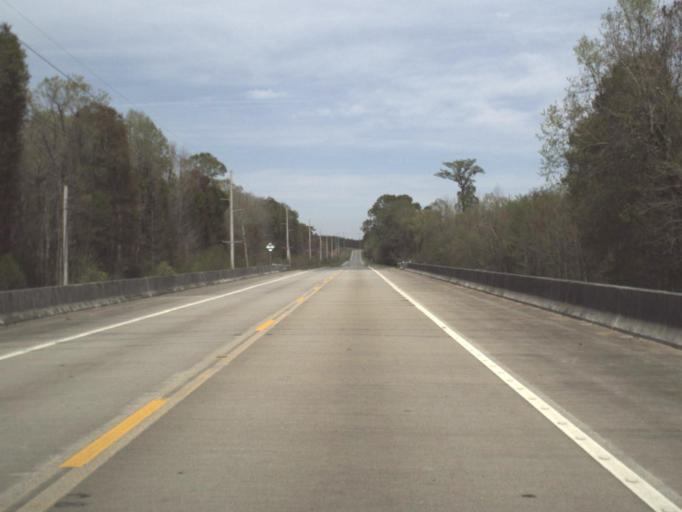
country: US
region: Alabama
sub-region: Houston County
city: Cottonwood
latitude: 30.9373
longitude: -85.2954
